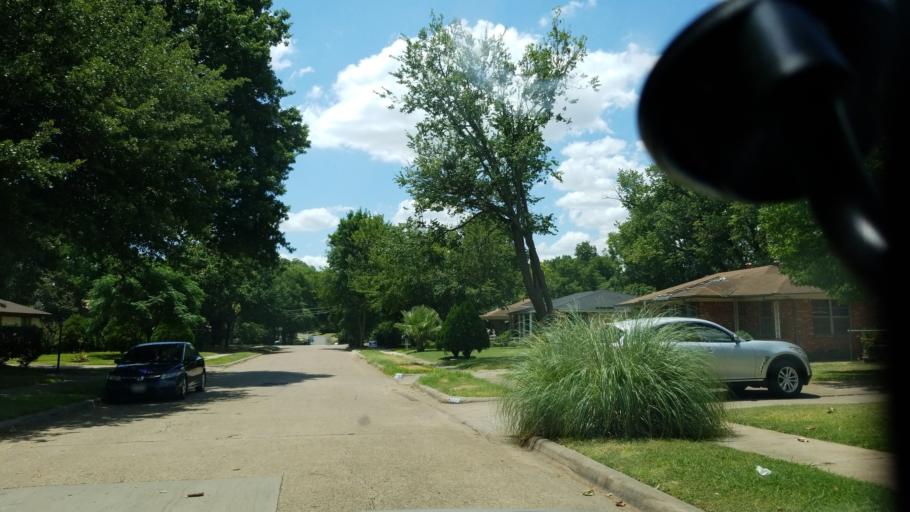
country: US
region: Texas
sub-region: Dallas County
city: Cockrell Hill
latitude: 32.7100
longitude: -96.8474
